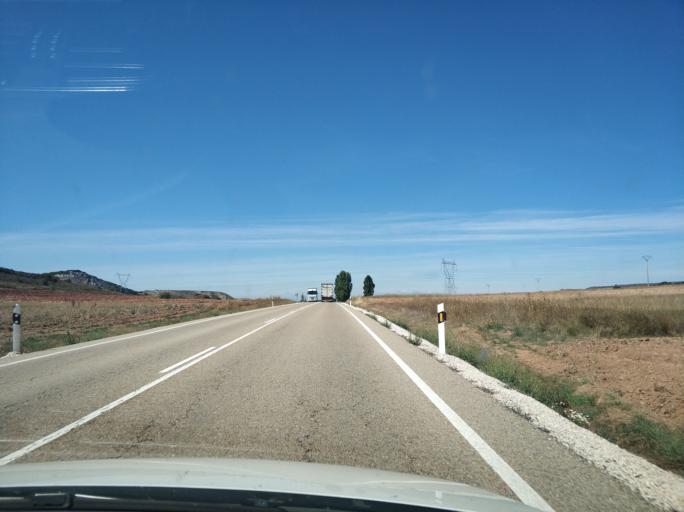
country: ES
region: Castille and Leon
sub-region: Provincia de Burgos
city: Montorio
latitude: 42.6060
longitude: -3.8022
